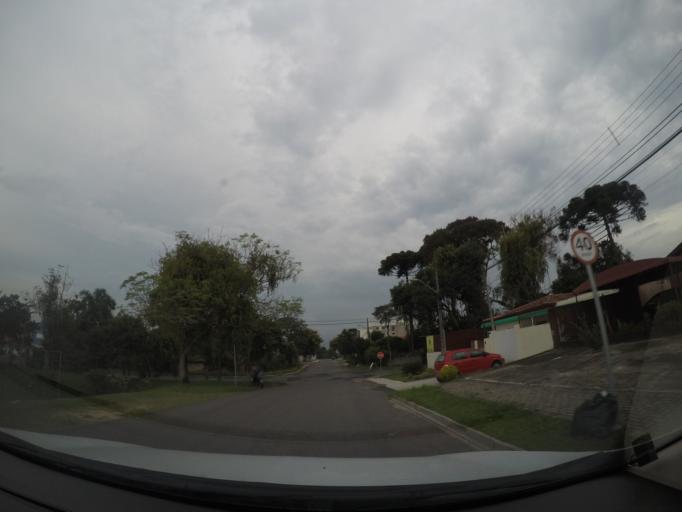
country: BR
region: Parana
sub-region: Sao Jose Dos Pinhais
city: Sao Jose dos Pinhais
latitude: -25.5138
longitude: -49.2370
